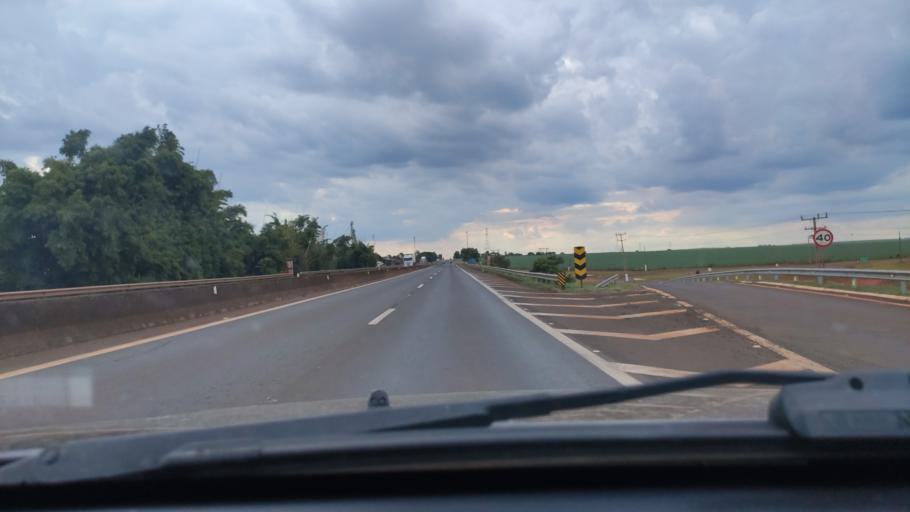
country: BR
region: Sao Paulo
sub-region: Palmital
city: Palmital
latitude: -22.8154
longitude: -50.0544
